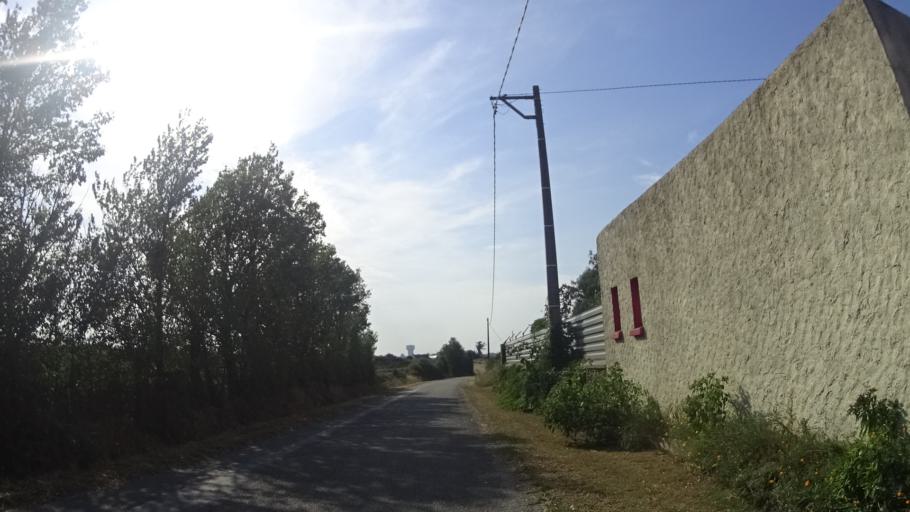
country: FR
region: Pays de la Loire
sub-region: Departement de la Loire-Atlantique
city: Donges
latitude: 47.3248
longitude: -2.1060
